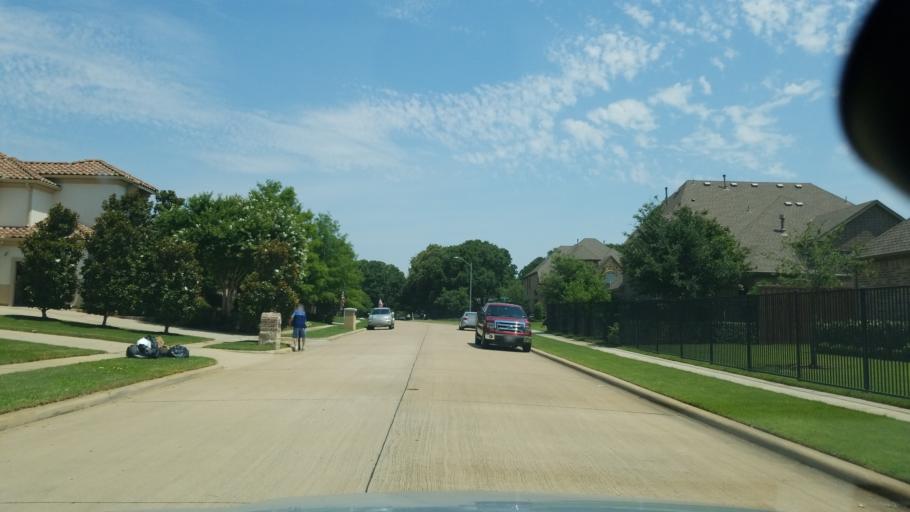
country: US
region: Texas
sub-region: Dallas County
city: Irving
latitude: 32.8484
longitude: -96.9435
